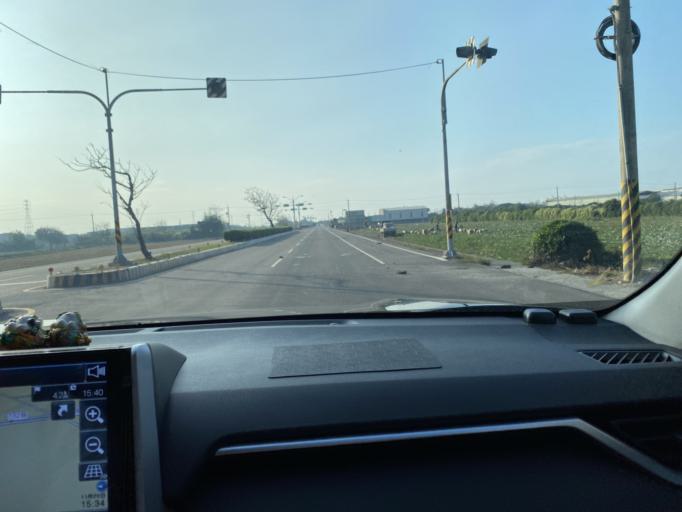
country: TW
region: Taiwan
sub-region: Changhua
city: Chang-hua
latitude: 23.9618
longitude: 120.3791
